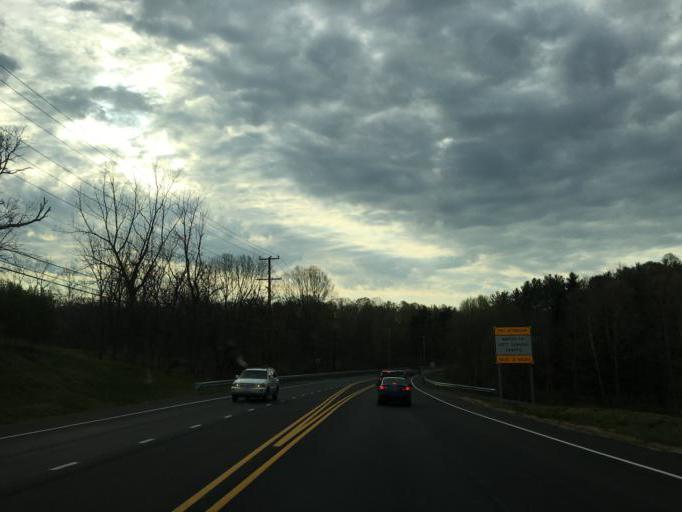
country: US
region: Maryland
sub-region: Carroll County
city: Sykesville
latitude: 39.3490
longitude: -76.9623
